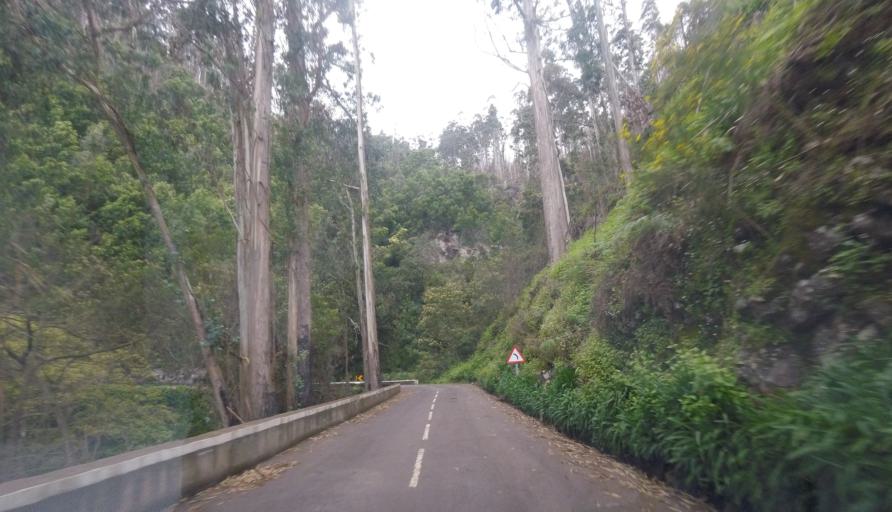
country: PT
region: Madeira
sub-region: Funchal
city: Nossa Senhora do Monte
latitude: 32.6901
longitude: -16.8894
